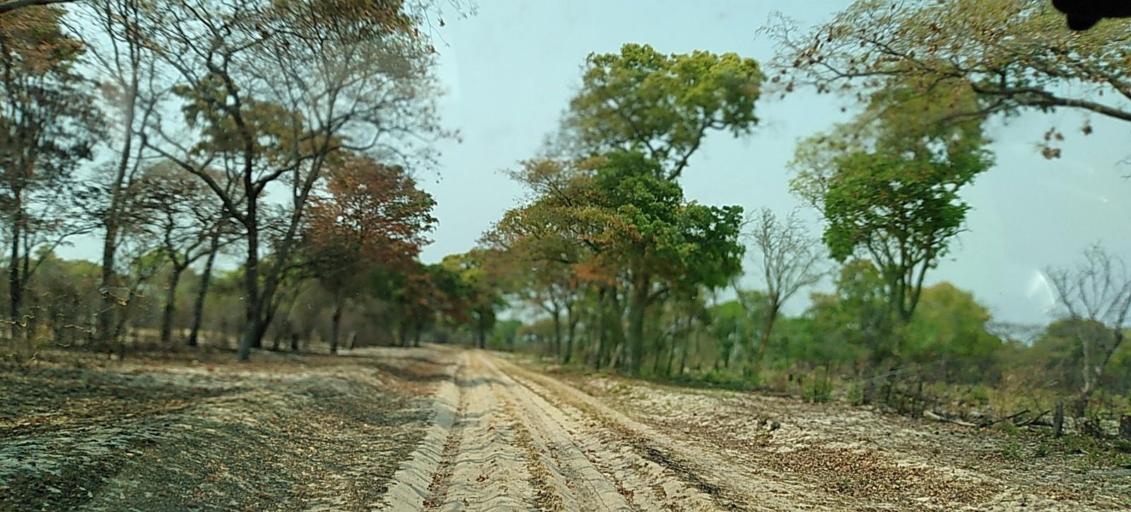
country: ZM
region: North-Western
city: Zambezi
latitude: -13.9397
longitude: 23.2223
